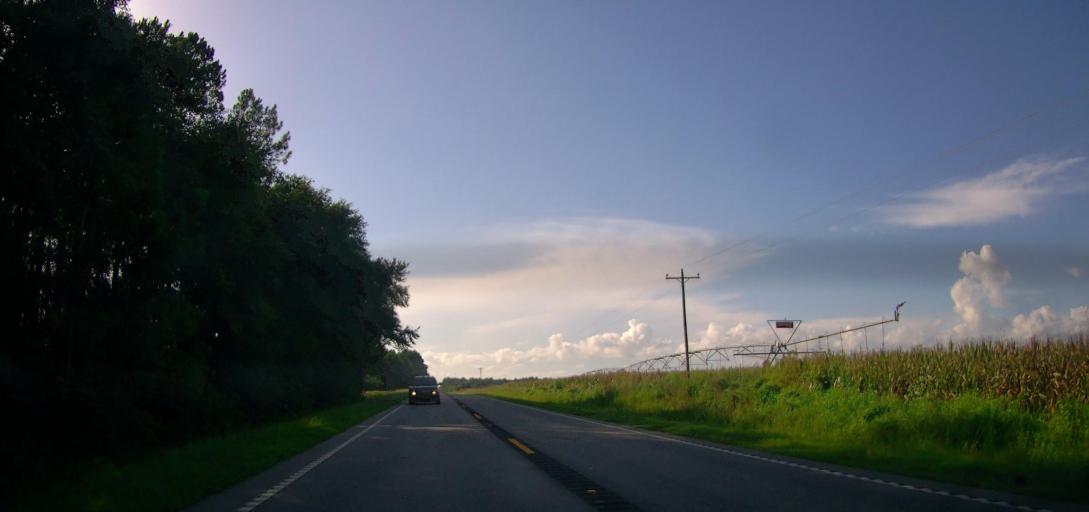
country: US
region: Georgia
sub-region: Coffee County
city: Nicholls
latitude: 31.4333
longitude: -82.7071
